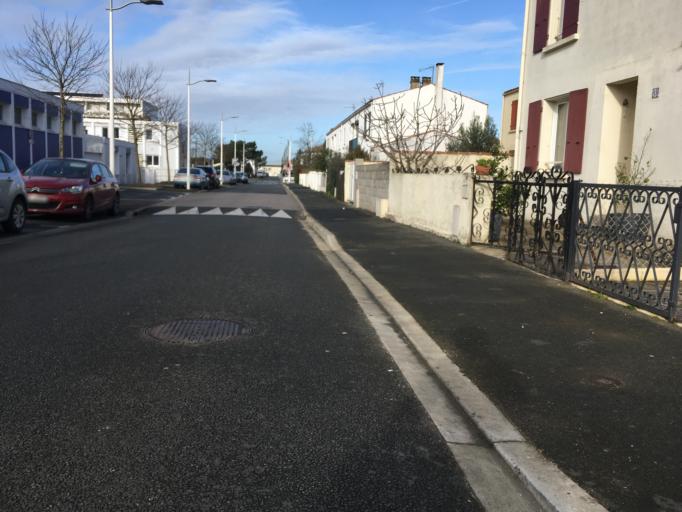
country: FR
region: Poitou-Charentes
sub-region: Departement de la Charente-Maritime
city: La Rochelle
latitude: 46.1716
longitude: -1.1784
